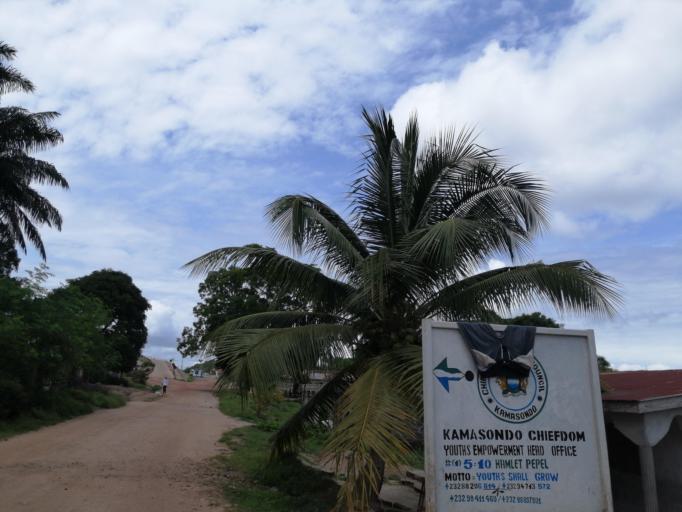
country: SL
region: Northern Province
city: Pepel
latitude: 8.5923
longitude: -13.0571
